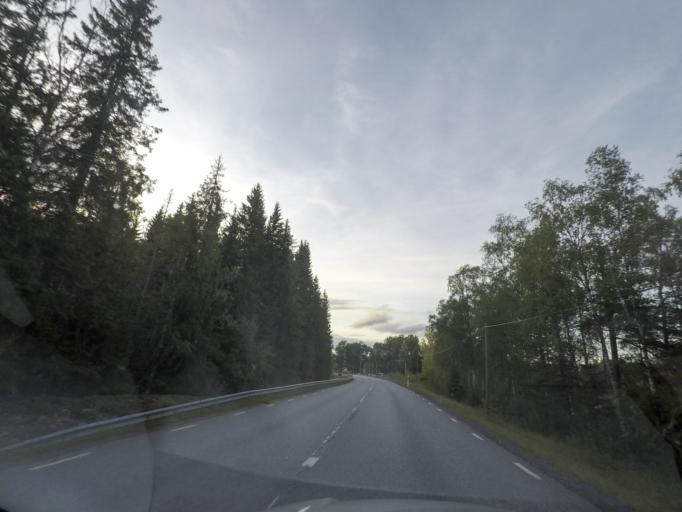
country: SE
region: OErebro
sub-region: Nora Kommun
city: As
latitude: 59.5591
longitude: 14.7429
